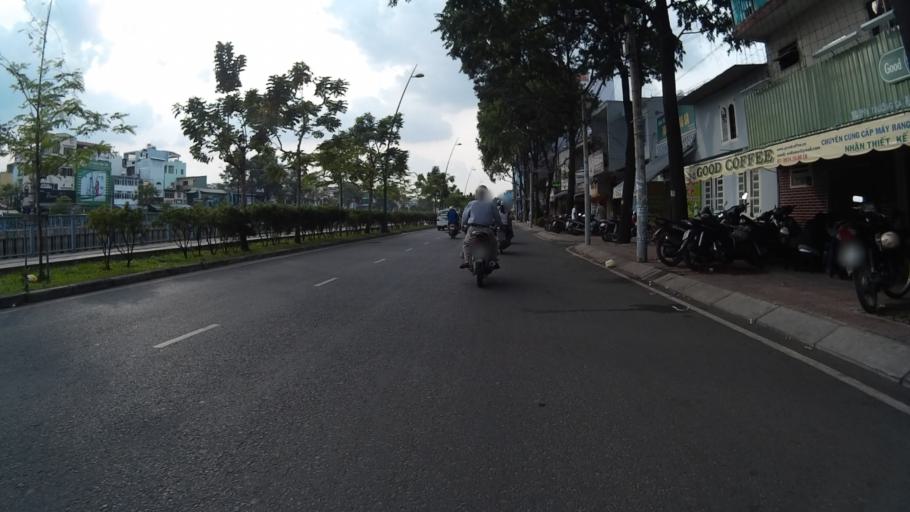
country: VN
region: Ho Chi Minh City
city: Quan Phu Nhuan
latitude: 10.7871
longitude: 106.6743
